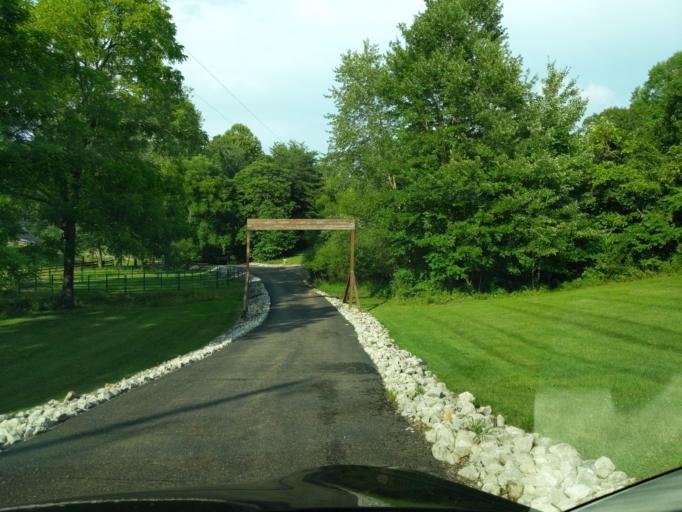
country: US
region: Ohio
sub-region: Fairfield County
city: Lancaster
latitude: 39.5516
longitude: -82.6467
